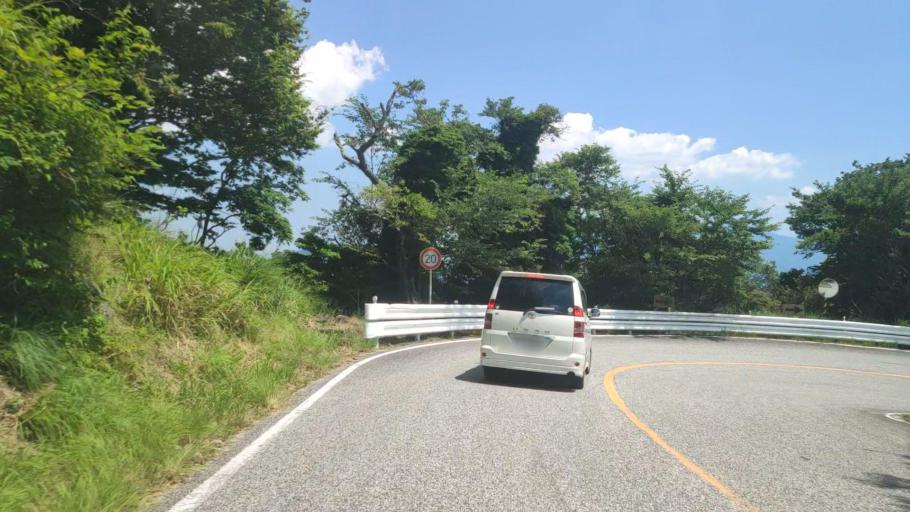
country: JP
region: Gifu
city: Tarui
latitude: 35.3805
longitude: 136.4529
